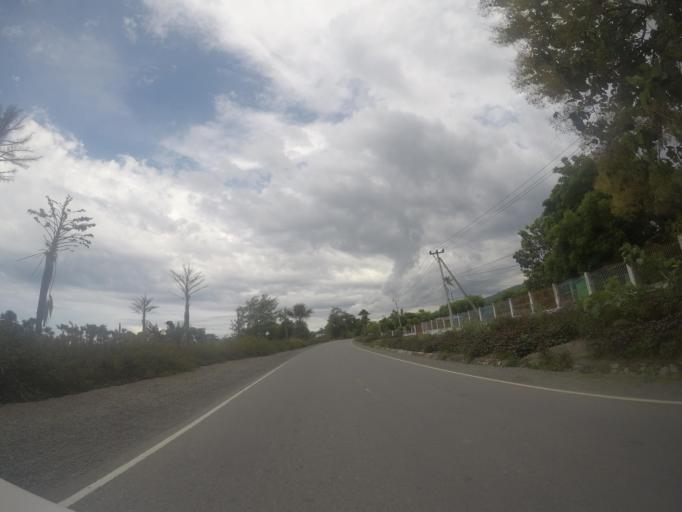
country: TL
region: Liquica
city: Liquica
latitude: -8.6039
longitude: 125.2965
